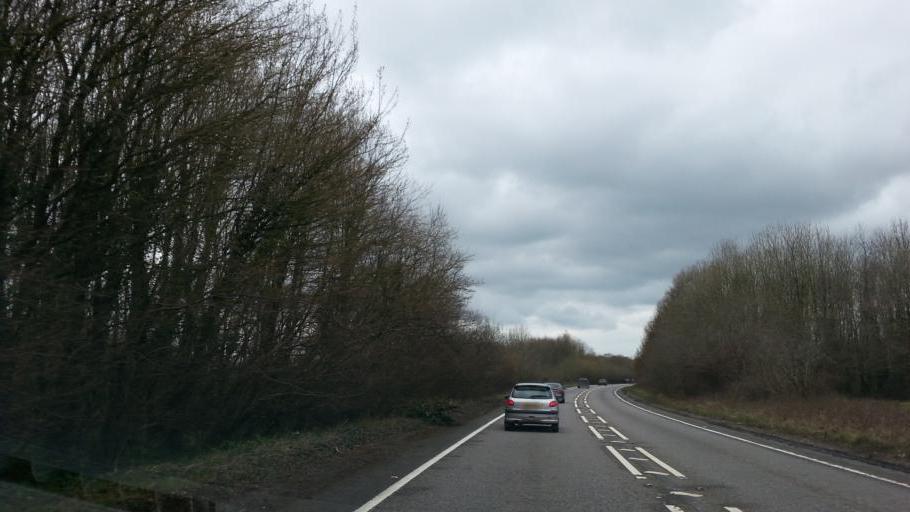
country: GB
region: England
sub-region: Devon
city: Barnstaple
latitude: 51.0580
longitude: -3.9733
